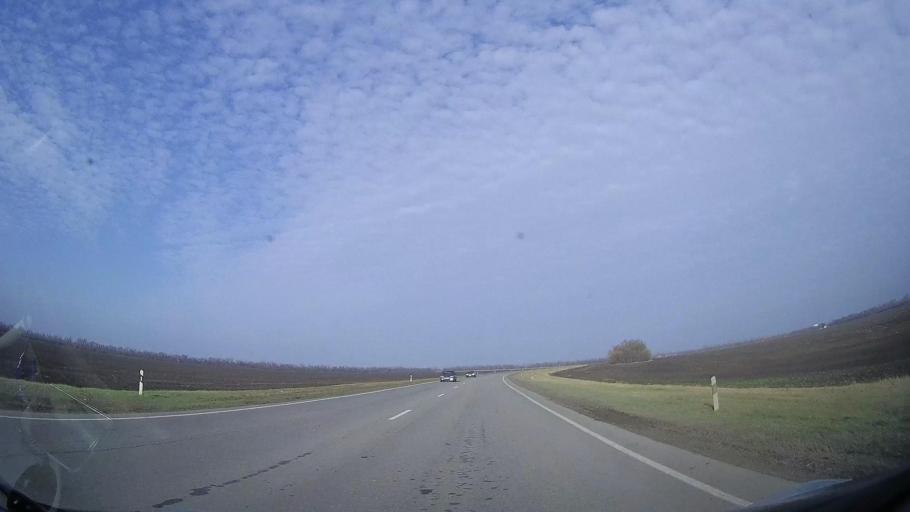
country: RU
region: Rostov
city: Tselina
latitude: 46.5179
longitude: 40.9944
